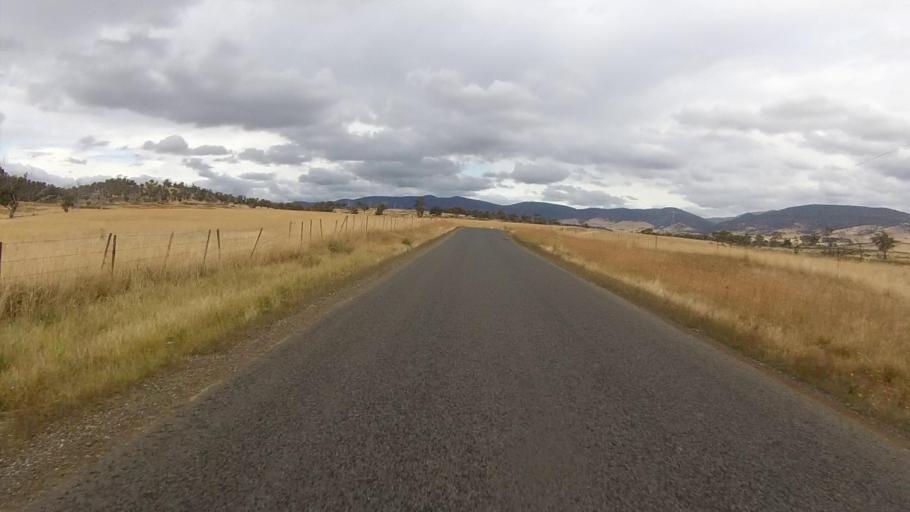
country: AU
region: Tasmania
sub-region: Northern Midlands
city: Evandale
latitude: -41.8028
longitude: 147.7523
